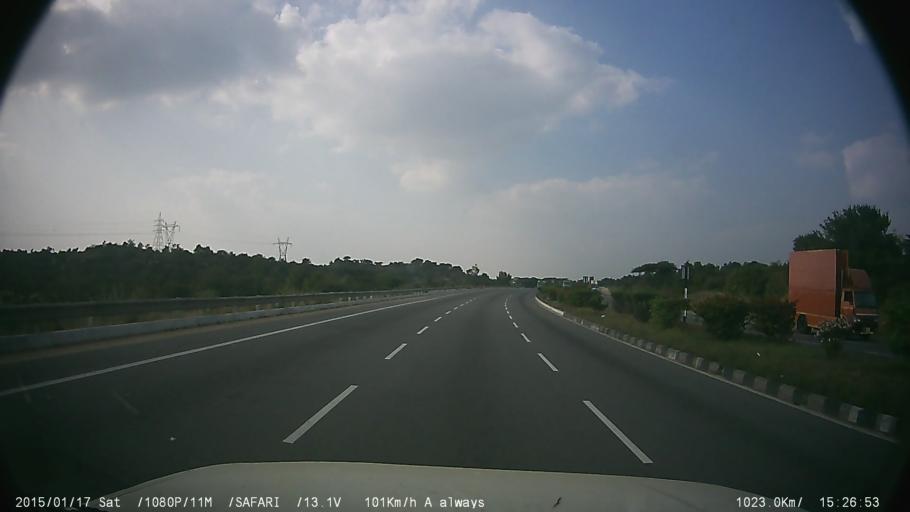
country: IN
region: Tamil Nadu
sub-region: Krishnagiri
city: Krishnagiri
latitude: 12.6323
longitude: 78.0738
